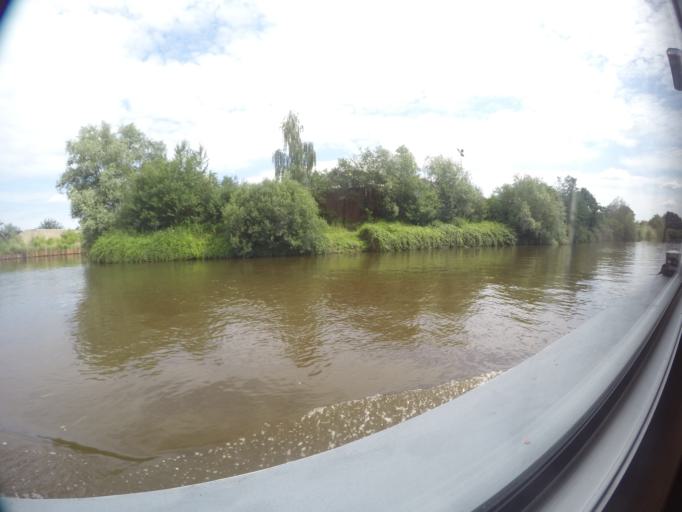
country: NL
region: Overijssel
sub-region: Gemeente Hengelo
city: Hengelo
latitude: 52.2483
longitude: 6.7850
